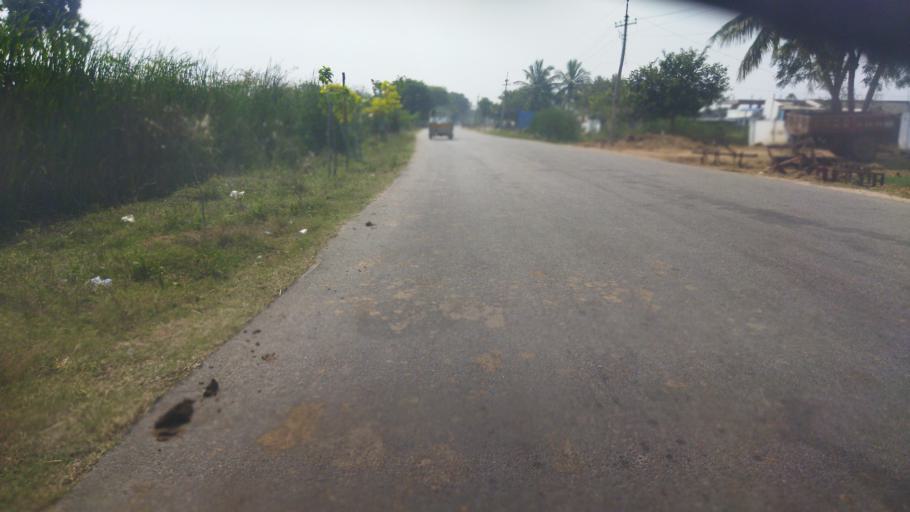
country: IN
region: Telangana
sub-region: Nalgonda
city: Nalgonda
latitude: 17.1515
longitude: 79.3105
